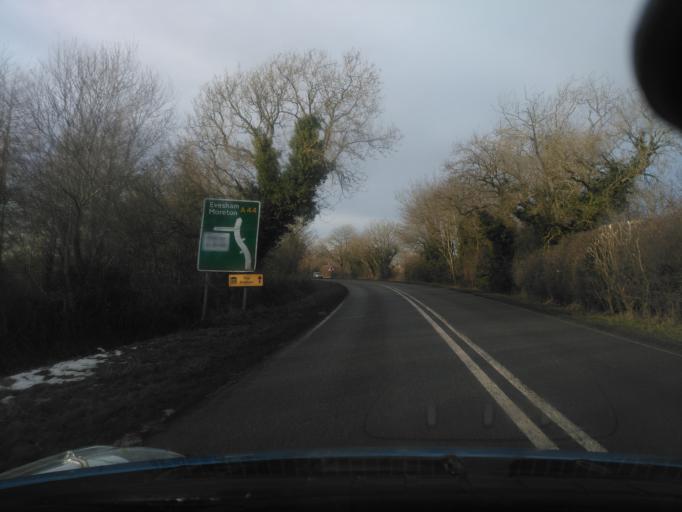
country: GB
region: England
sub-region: Oxfordshire
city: Chipping Norton
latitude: 51.9571
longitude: -1.6040
